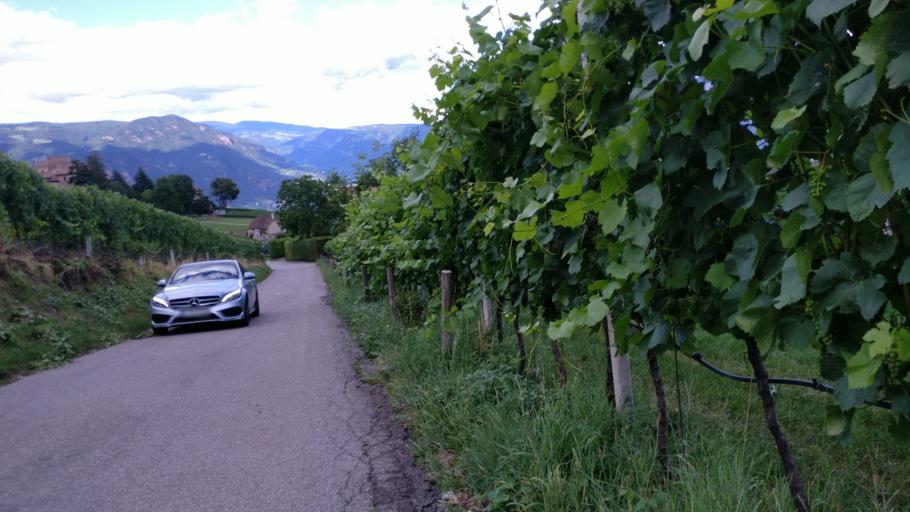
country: IT
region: Trentino-Alto Adige
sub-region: Bolzano
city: San Michele
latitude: 46.4597
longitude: 11.2441
